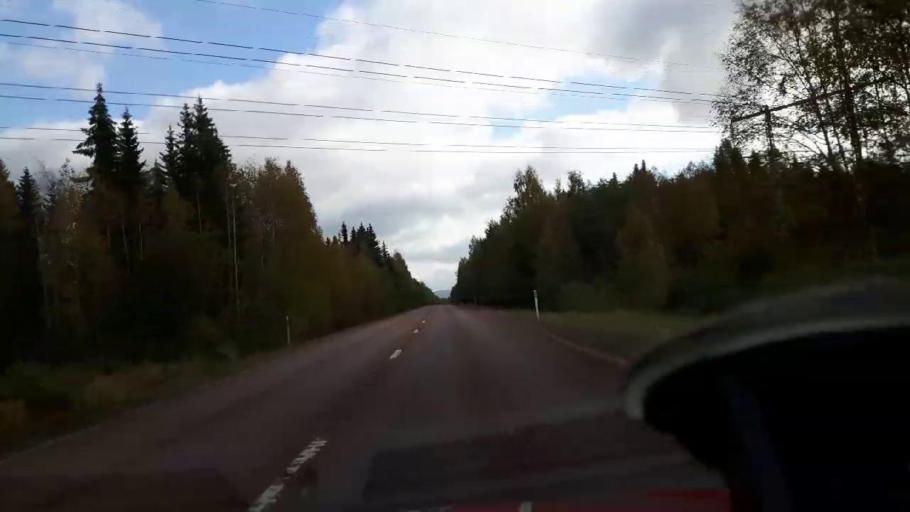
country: SE
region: Gaevleborg
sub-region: Ljusdals Kommun
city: Jaervsoe
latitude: 61.6376
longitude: 16.2462
